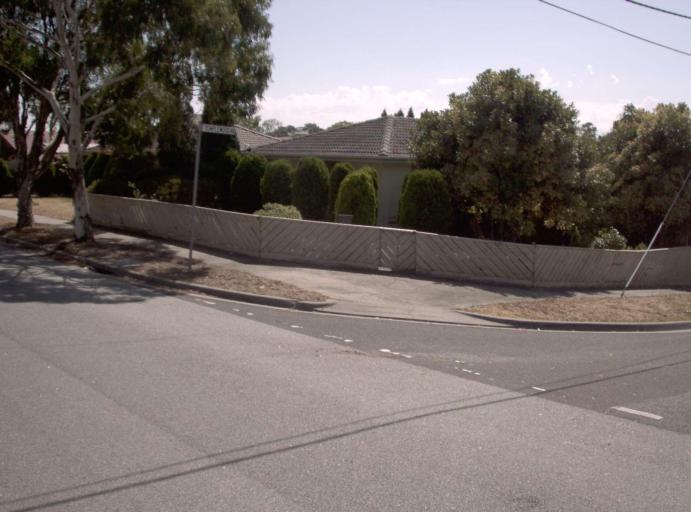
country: AU
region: Victoria
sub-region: Greater Dandenong
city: Noble Park North
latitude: -37.9511
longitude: 145.1915
